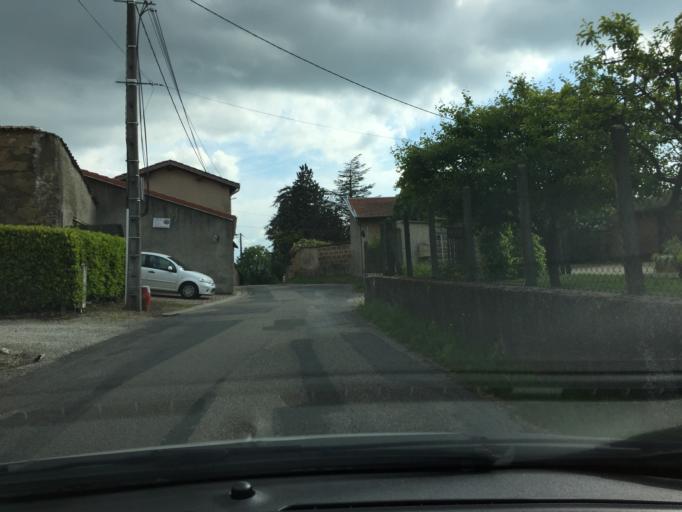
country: FR
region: Rhone-Alpes
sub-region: Departement du Rhone
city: Orlienas
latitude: 45.6635
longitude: 4.7195
